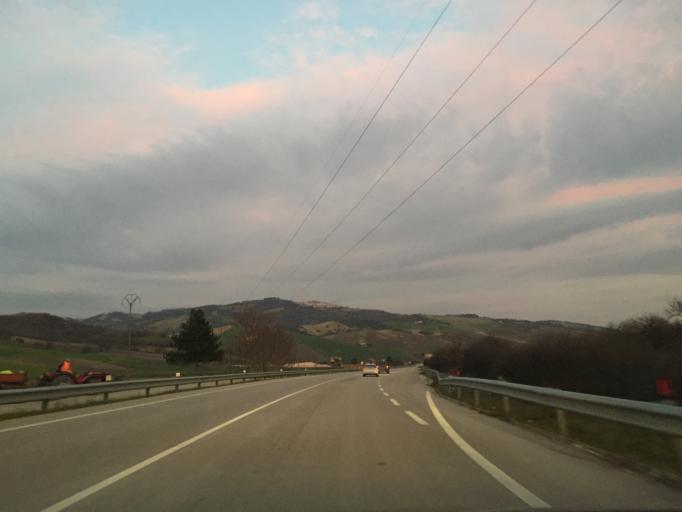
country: IT
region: Apulia
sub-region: Provincia di Foggia
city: Celenza Valfortore
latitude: 41.5266
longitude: 14.9586
